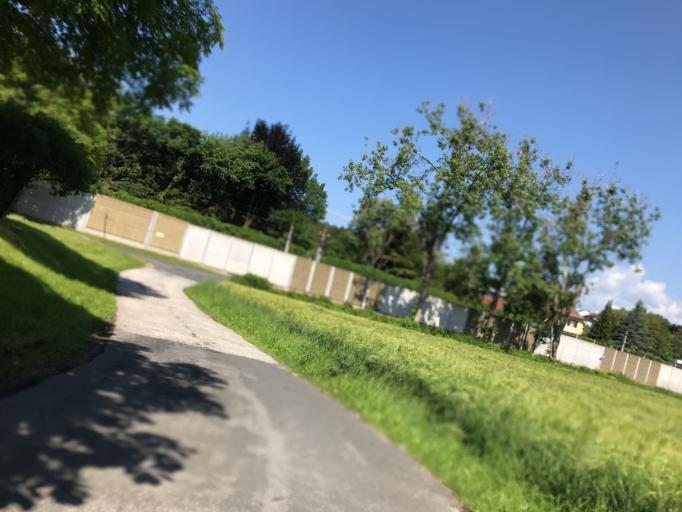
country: AT
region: Carinthia
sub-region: Villach Stadt
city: Villach
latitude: 46.5904
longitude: 13.8304
